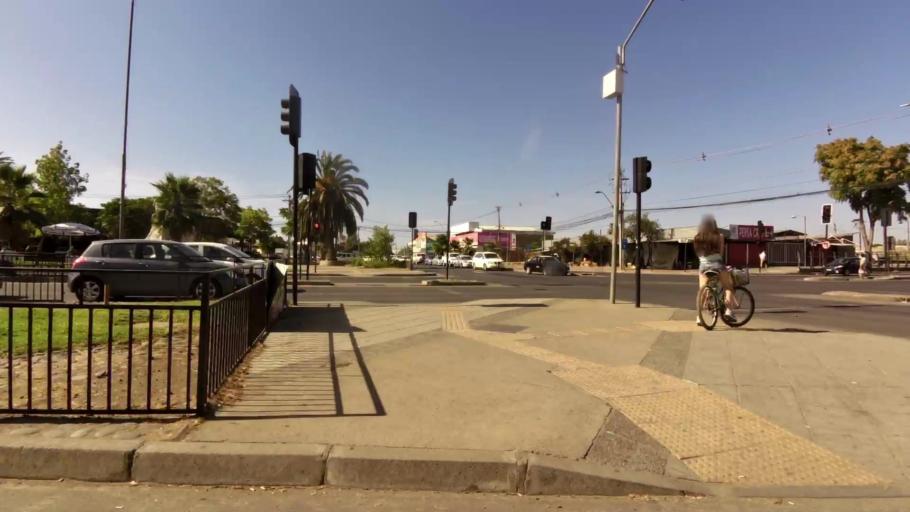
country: CL
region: Maule
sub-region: Provincia de Talca
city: Talca
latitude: -35.4233
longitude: -71.6498
